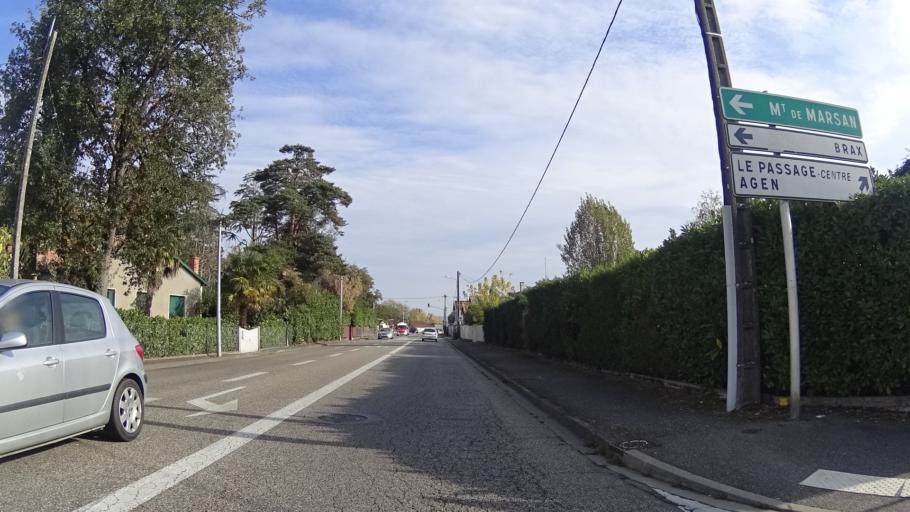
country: FR
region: Aquitaine
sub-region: Departement du Lot-et-Garonne
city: Le Passage
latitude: 44.1925
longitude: 0.5917
